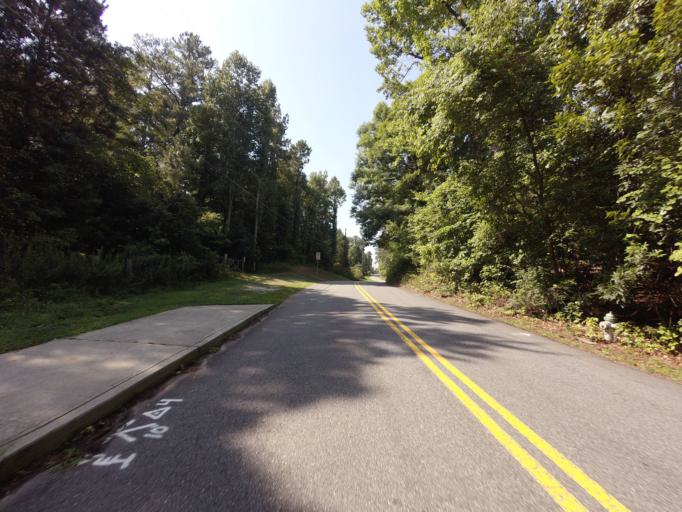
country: US
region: Georgia
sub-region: Fulton County
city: Johns Creek
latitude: 34.0691
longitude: -84.2150
